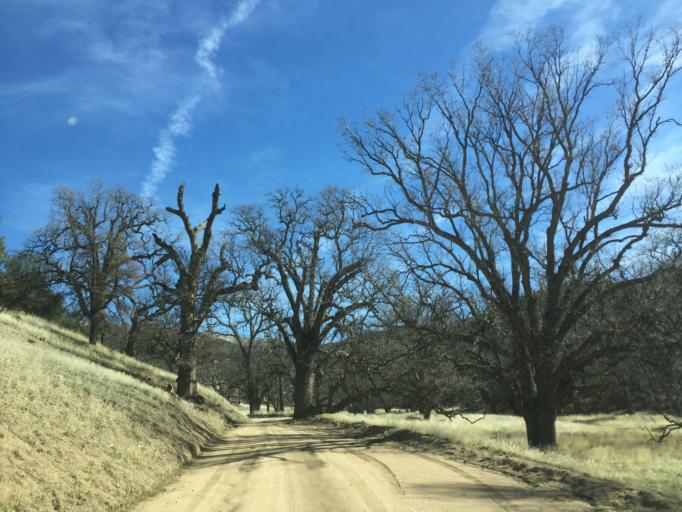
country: US
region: California
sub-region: Kern County
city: Stallion Springs
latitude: 34.9144
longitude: -118.6915
